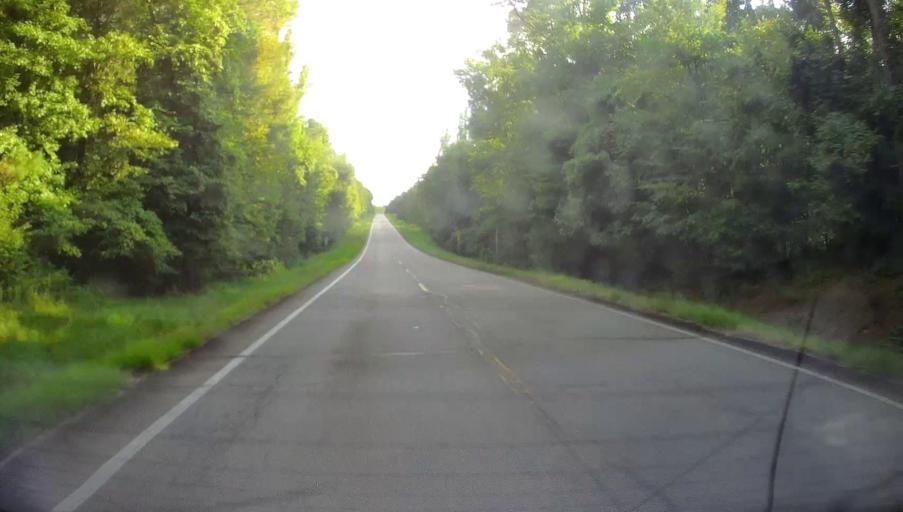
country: US
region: Georgia
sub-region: Crawford County
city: Knoxville
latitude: 32.8240
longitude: -84.0206
